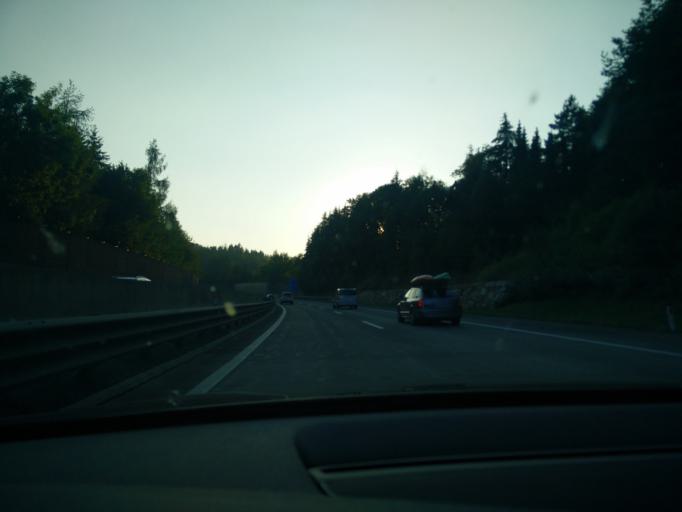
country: AT
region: Carinthia
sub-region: Politischer Bezirk Klagenfurt Land
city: Maria Worth
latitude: 46.6411
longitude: 14.1362
